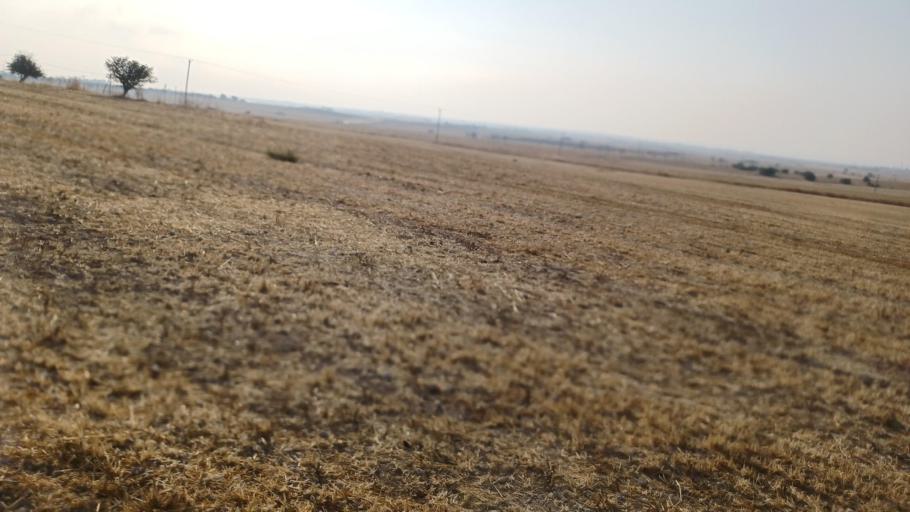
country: CY
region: Larnaka
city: Tersefanou
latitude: 34.8349
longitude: 33.5162
